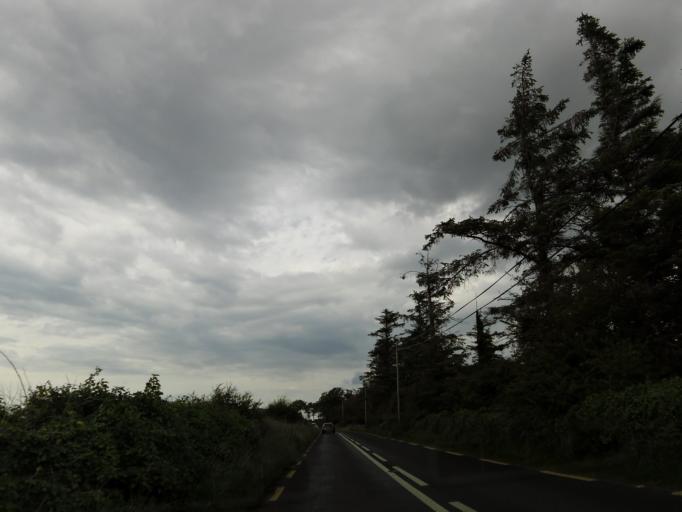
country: IE
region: Connaught
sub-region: County Galway
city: Gaillimh
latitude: 53.1340
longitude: -9.0666
